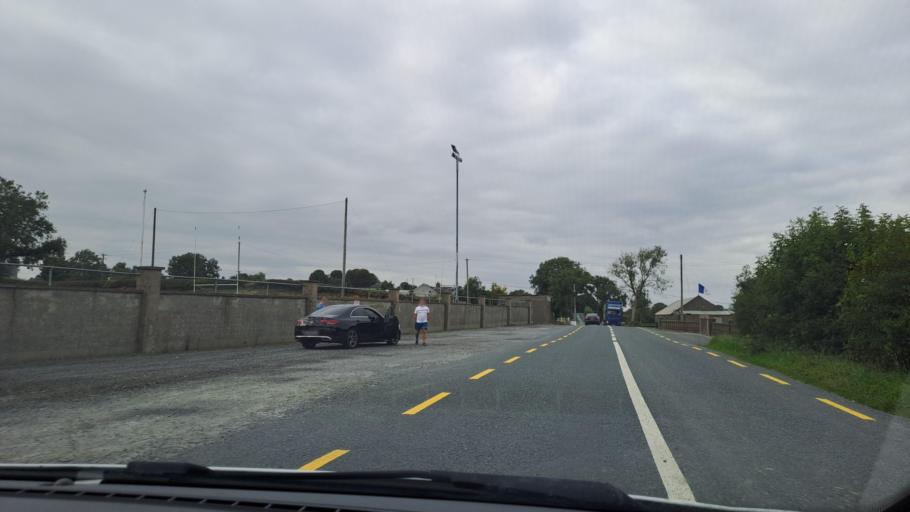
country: IE
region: Ulster
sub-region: An Cabhan
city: Kingscourt
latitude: 53.9803
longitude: -6.8793
